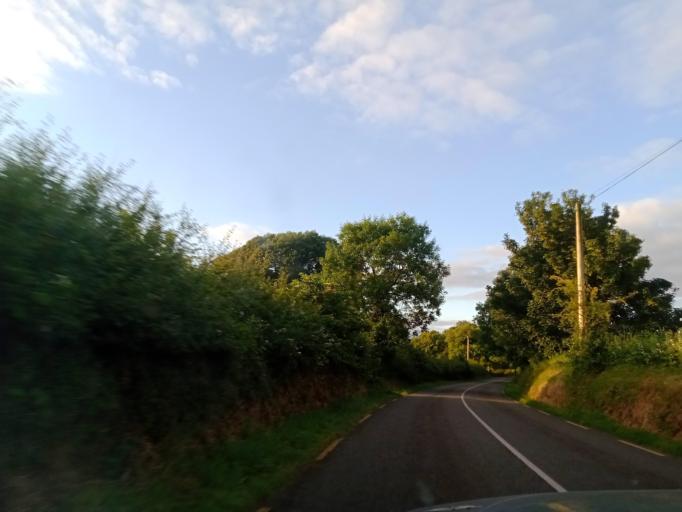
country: IE
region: Leinster
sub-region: Kilkenny
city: Castlecomer
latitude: 52.8487
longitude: -7.1774
